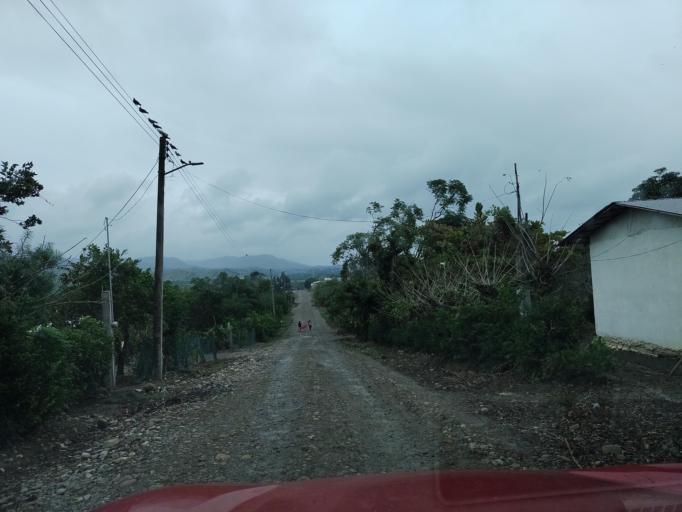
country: MX
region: Veracruz
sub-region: Papantla
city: El Chote
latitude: 20.4136
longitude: -97.3666
